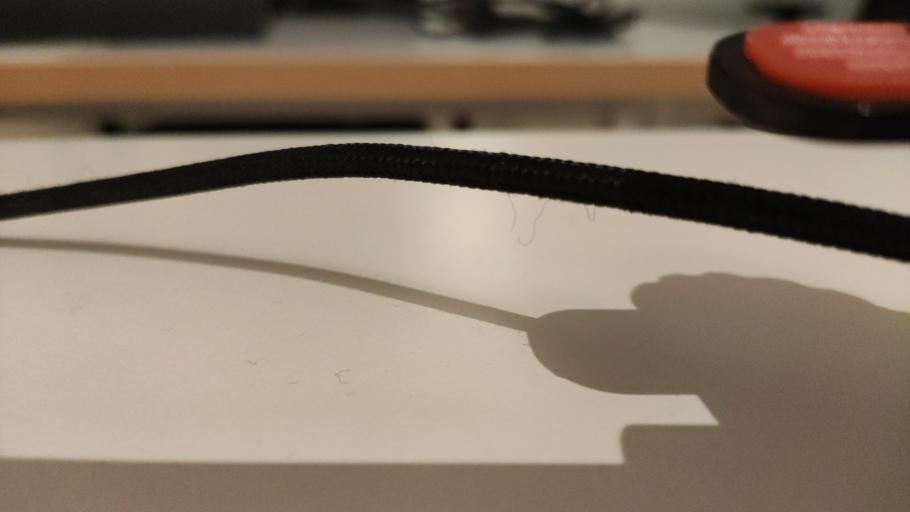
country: RU
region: Moskovskaya
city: Il'inskiy Pogost
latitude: 55.5285
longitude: 38.8723
